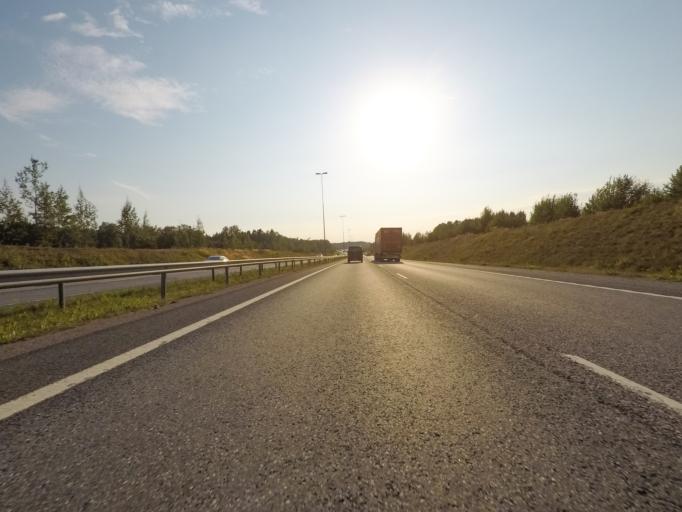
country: FI
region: Uusimaa
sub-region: Helsinki
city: Lohja
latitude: 60.2847
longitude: 24.1390
